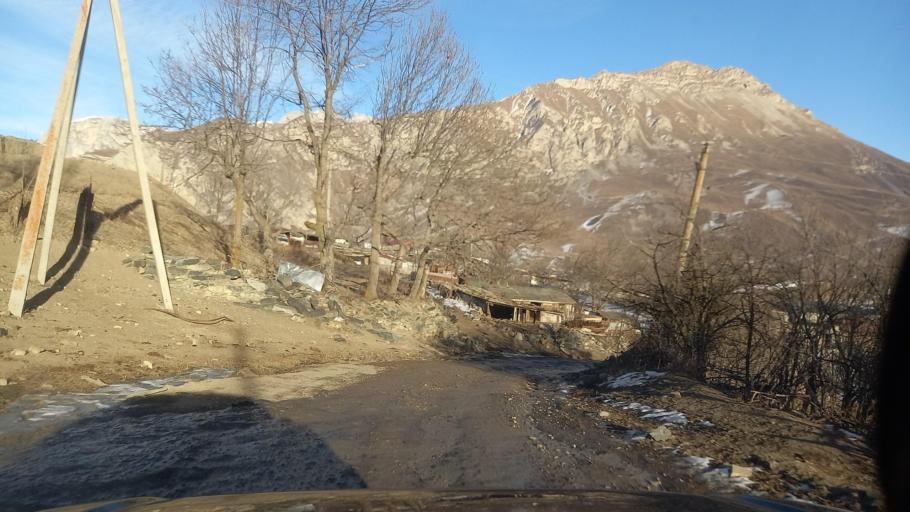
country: RU
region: Ingushetiya
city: Dzhayrakh
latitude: 42.8430
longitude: 44.5066
